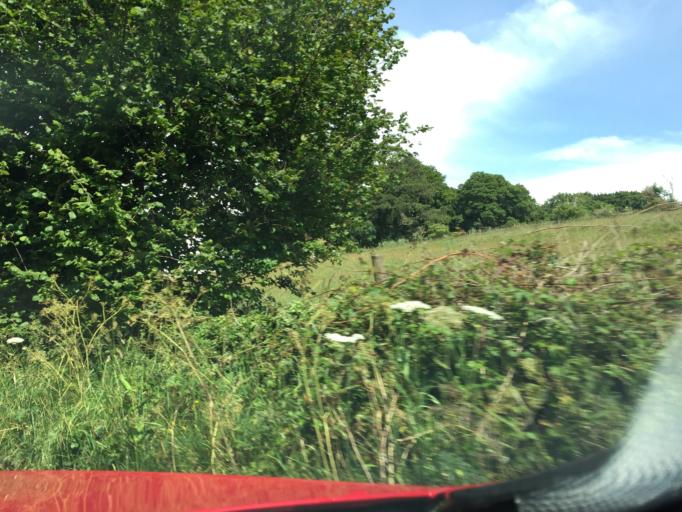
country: GB
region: England
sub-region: Gloucestershire
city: Tetbury
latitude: 51.6206
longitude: -2.2237
